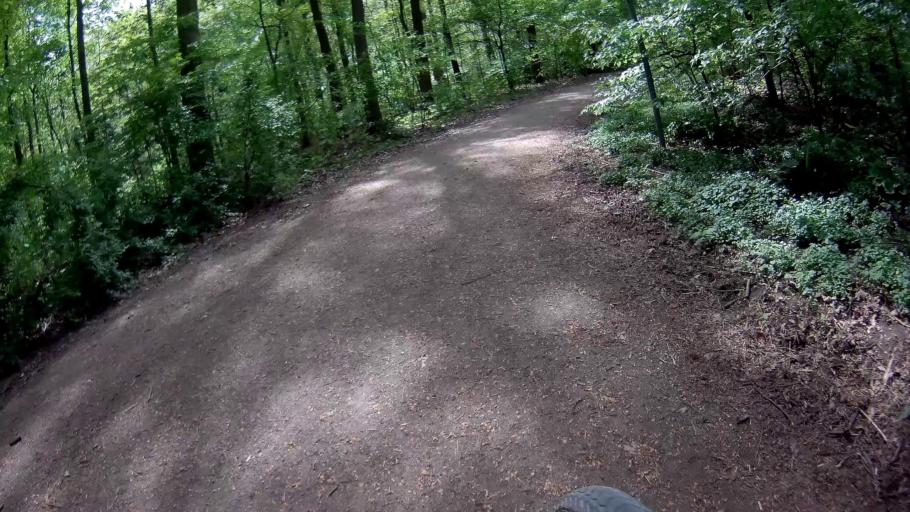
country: DE
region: North Rhine-Westphalia
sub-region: Regierungsbezirk Munster
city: Gelsenkirchen
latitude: 51.5575
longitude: 7.1038
